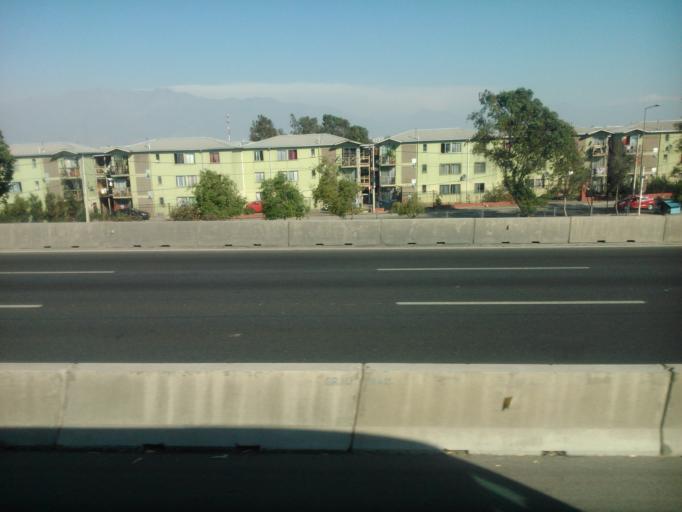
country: CL
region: Santiago Metropolitan
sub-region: Provincia de Santiago
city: Santiago
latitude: -33.4871
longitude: -70.6884
